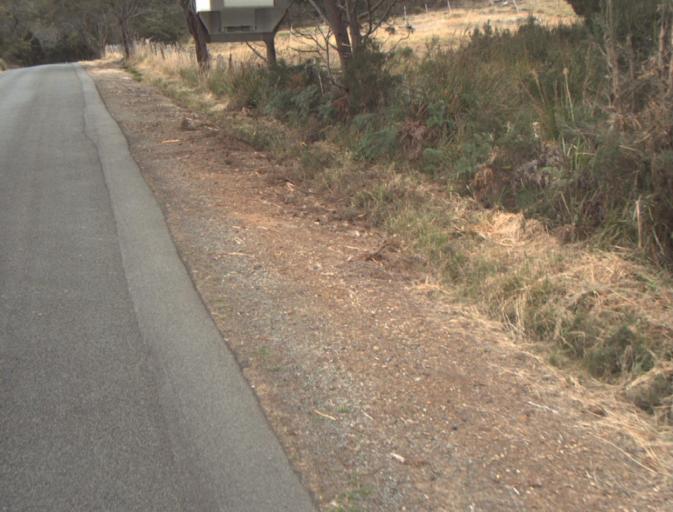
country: AU
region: Tasmania
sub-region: Launceston
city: Mayfield
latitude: -41.2834
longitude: 147.0259
